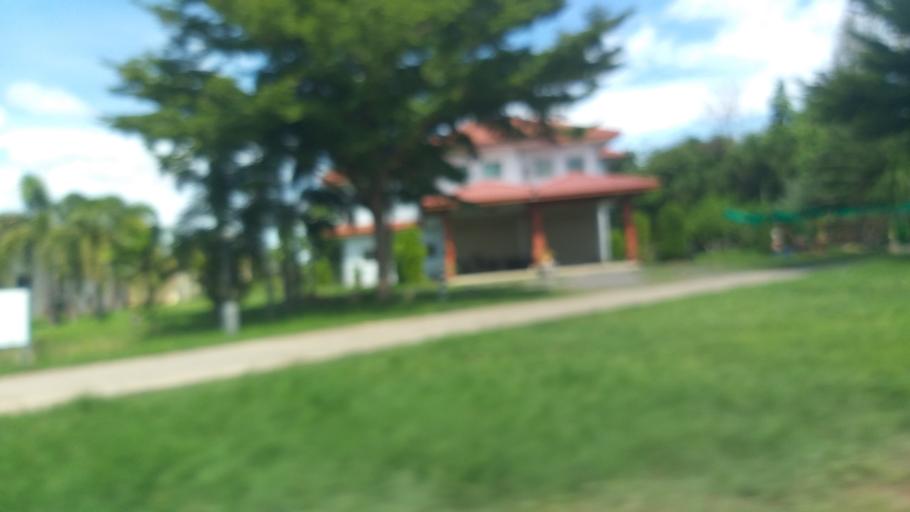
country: TH
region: Khon Kaen
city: Nong Ruea
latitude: 16.4568
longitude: 102.4412
